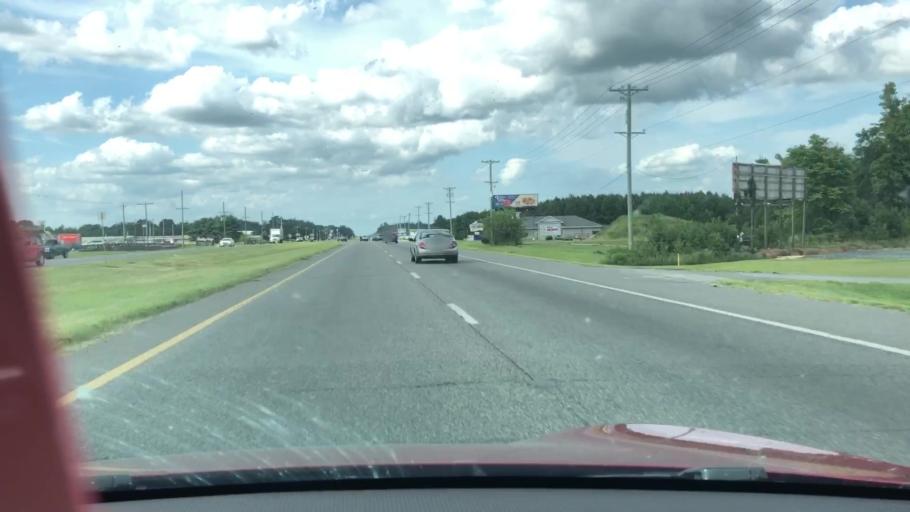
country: US
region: Delaware
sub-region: Sussex County
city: Seaford
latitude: 38.6641
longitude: -75.5935
